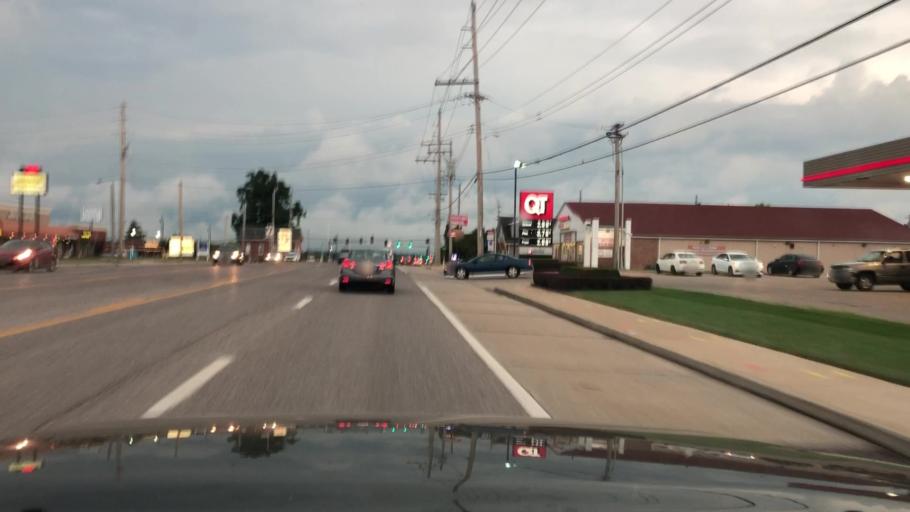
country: US
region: Missouri
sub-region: Saint Louis County
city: Bridgeton
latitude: 38.7414
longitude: -90.4059
